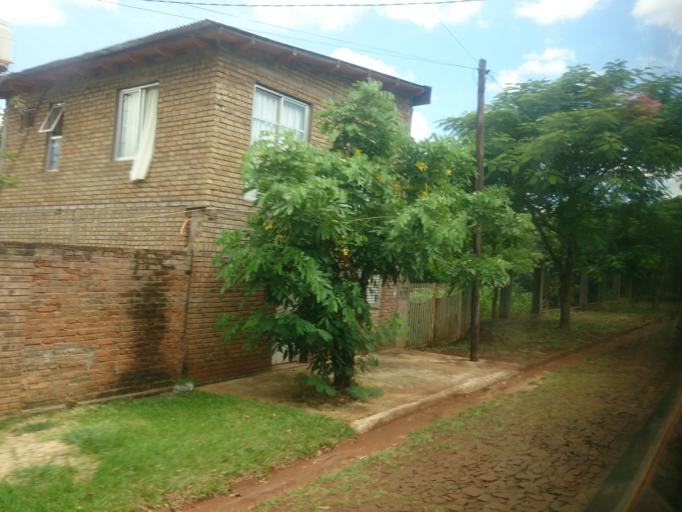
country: AR
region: Misiones
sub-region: Departamento de Obera
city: Obera
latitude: -27.4940
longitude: -55.1056
